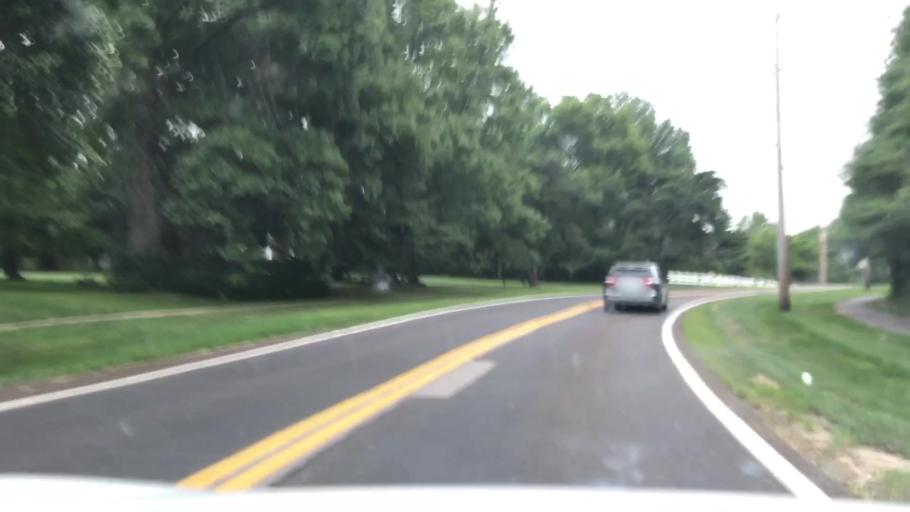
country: US
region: Missouri
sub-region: Saint Louis County
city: Clarkson Valley
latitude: 38.6268
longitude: -90.5921
